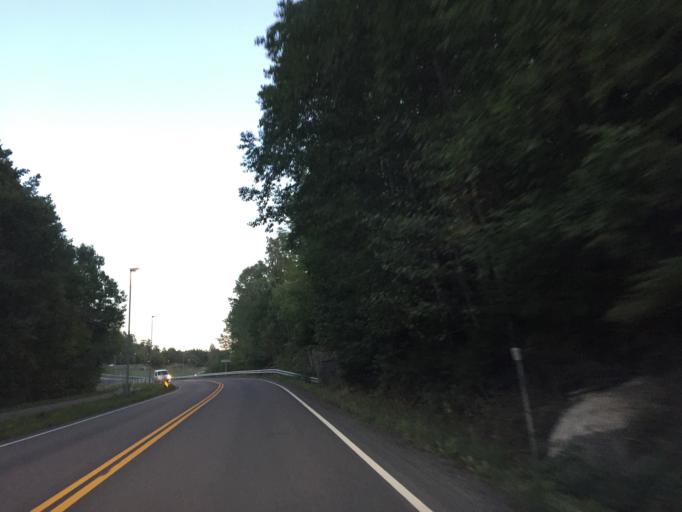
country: NO
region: Ostfold
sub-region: Moss
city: Moss
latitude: 59.5143
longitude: 10.6906
